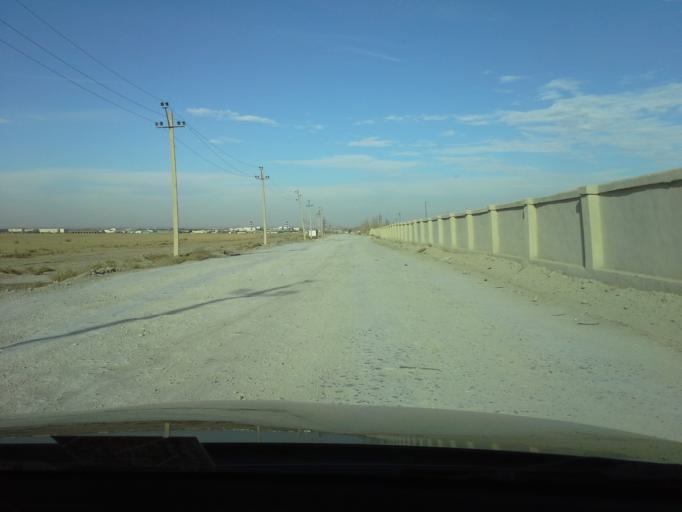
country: TM
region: Ahal
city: Abadan
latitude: 38.0353
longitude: 58.1605
